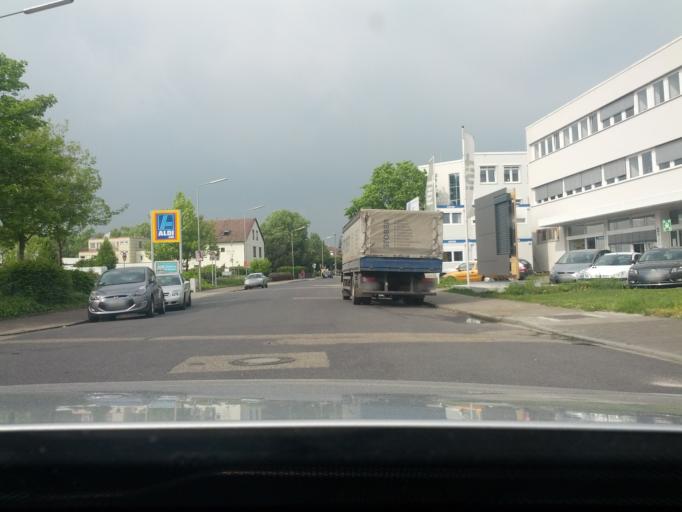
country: DE
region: Baden-Wuerttemberg
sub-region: Karlsruhe Region
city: Karlsruhe
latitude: 49.0087
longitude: 8.4397
